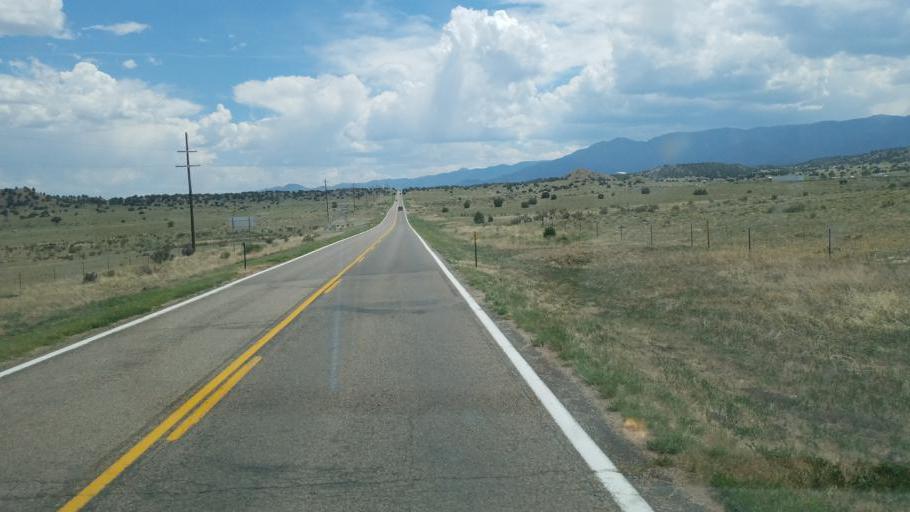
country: US
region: Colorado
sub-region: Fremont County
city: Florence
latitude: 38.3428
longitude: -105.1069
